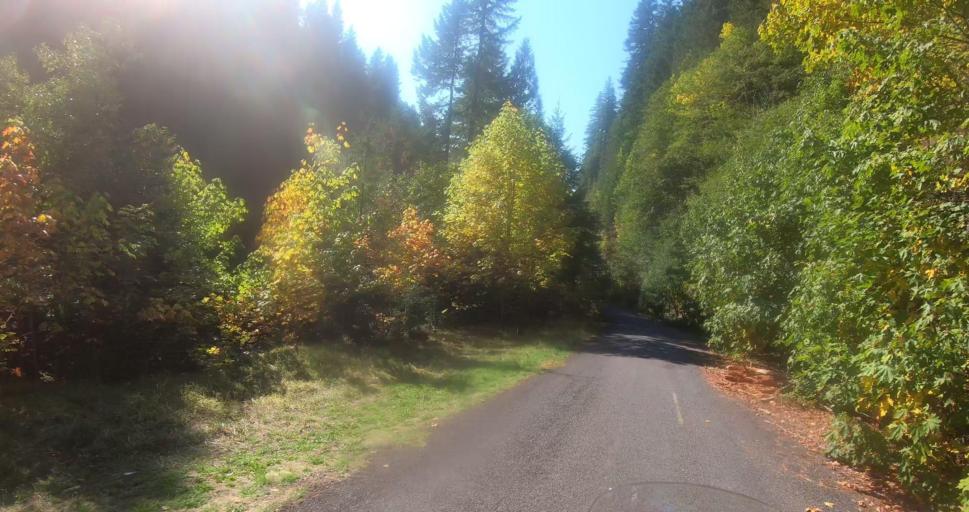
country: US
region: Washington
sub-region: Skamania County
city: Carson
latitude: 46.1853
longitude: -121.7958
